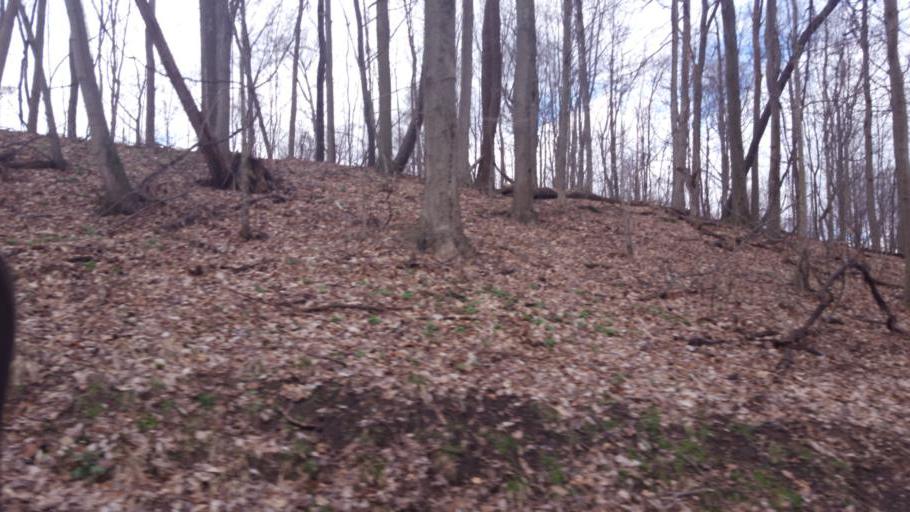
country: US
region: Ohio
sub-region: Sandusky County
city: Bellville
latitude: 40.5840
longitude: -82.4849
